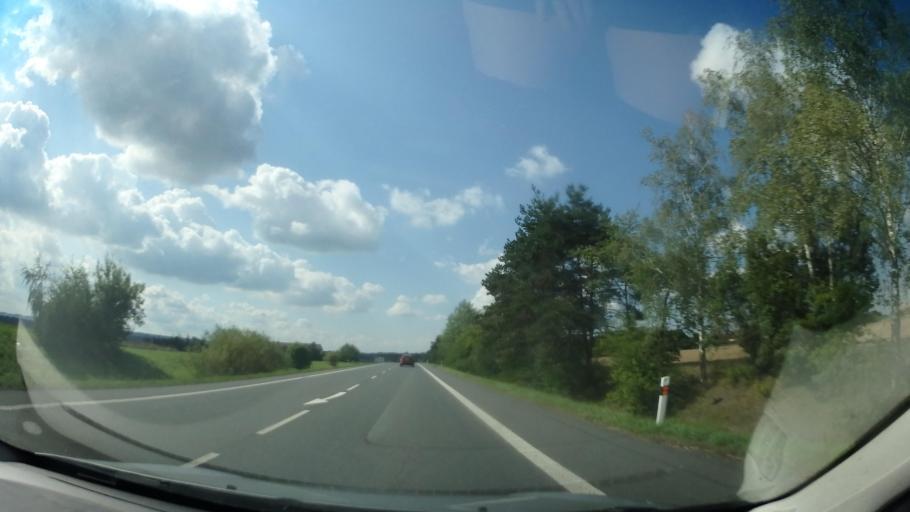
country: CZ
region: Central Bohemia
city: Kostelec nad Cernymi Lesy
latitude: 49.9853
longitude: 14.8555
